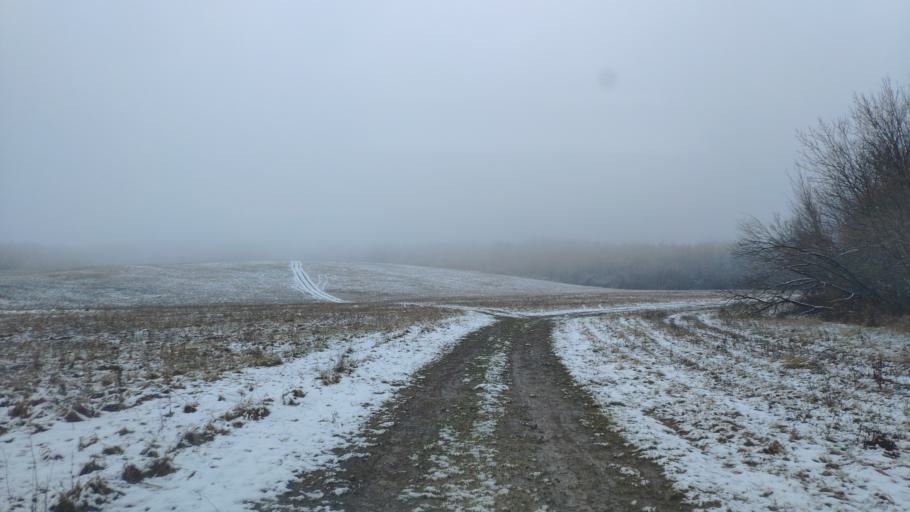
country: SK
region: Kosicky
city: Moldava nad Bodvou
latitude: 48.7365
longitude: 21.1008
